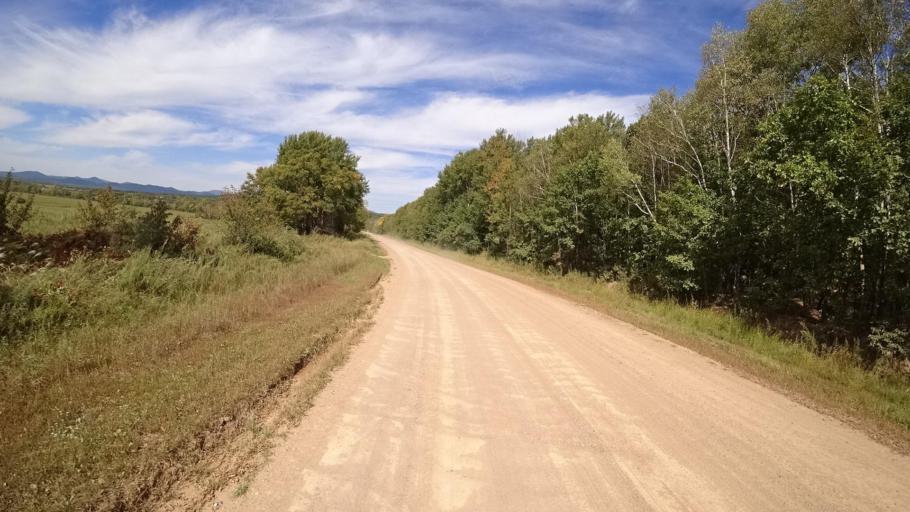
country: RU
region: Primorskiy
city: Yakovlevka
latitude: 44.6296
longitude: 133.6015
